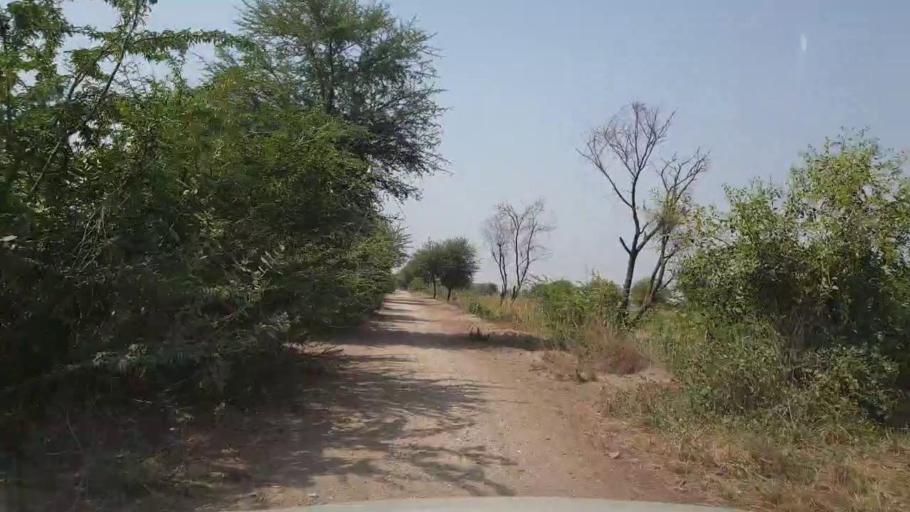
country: PK
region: Sindh
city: Dhoro Naro
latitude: 25.4888
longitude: 69.6485
